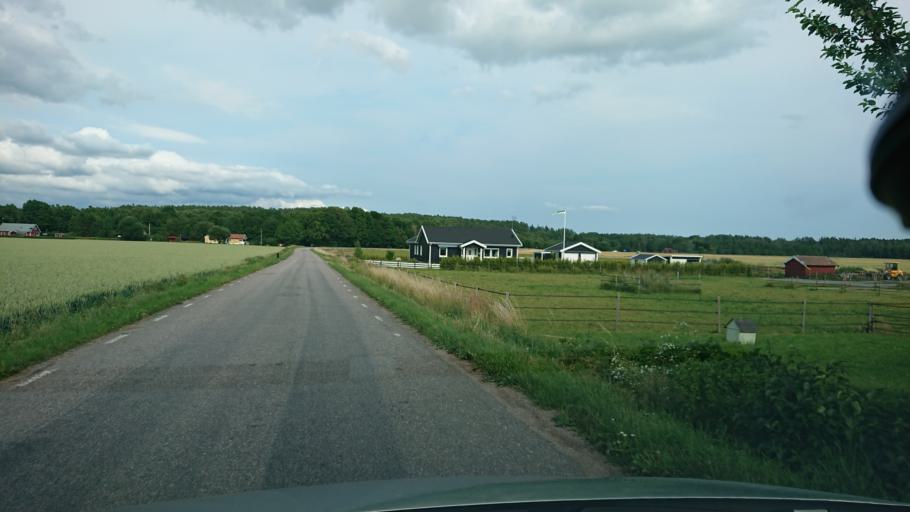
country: SE
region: Uppsala
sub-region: Osthammars Kommun
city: Bjorklinge
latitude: 59.9750
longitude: 17.5654
